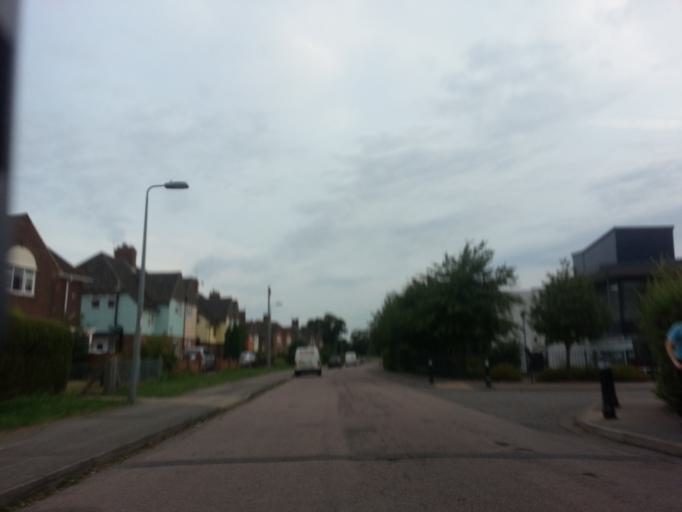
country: GB
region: England
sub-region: Suffolk
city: Ipswich
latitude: 52.0355
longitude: 1.1765
